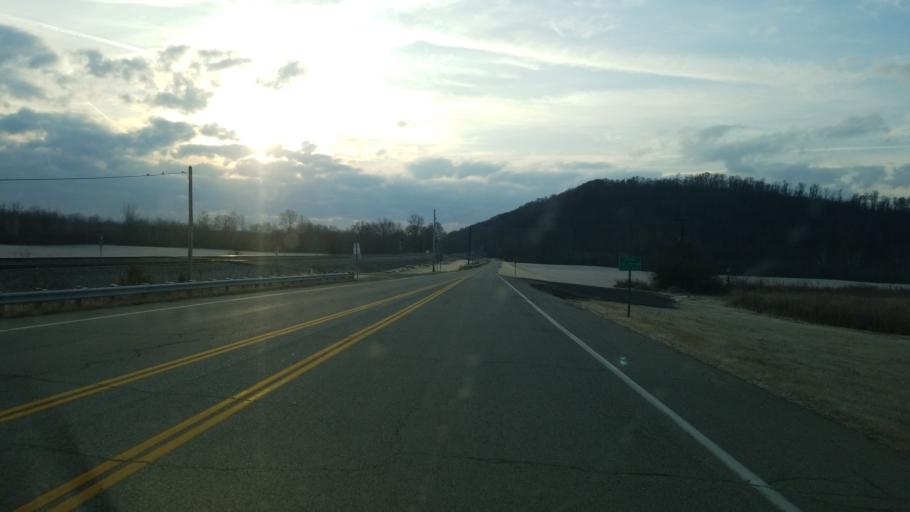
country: US
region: Ohio
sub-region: Ross County
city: Chillicothe
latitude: 39.2893
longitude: -82.9425
